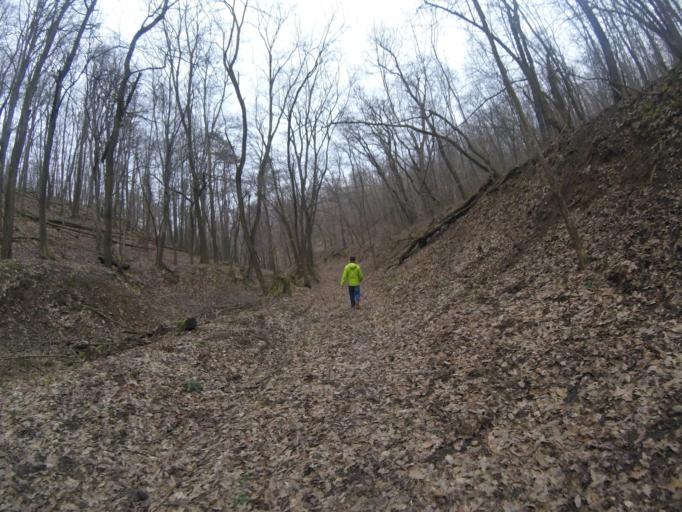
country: HU
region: Baranya
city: Mecseknadasd
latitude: 46.1395
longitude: 18.5210
